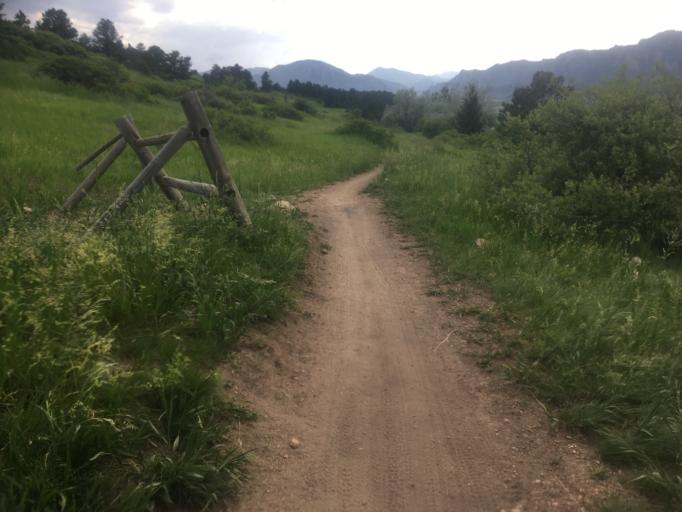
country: US
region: Colorado
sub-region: Boulder County
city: Superior
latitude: 39.9550
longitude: -105.2158
